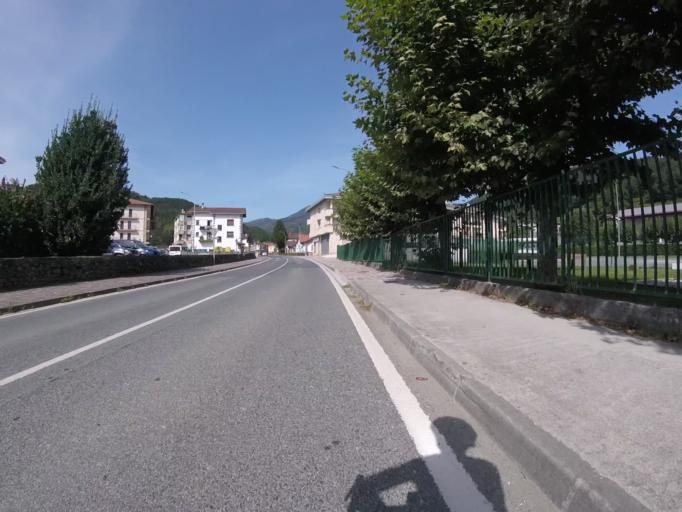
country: ES
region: Navarre
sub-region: Provincia de Navarra
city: Doneztebe
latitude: 43.1325
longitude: -1.6729
